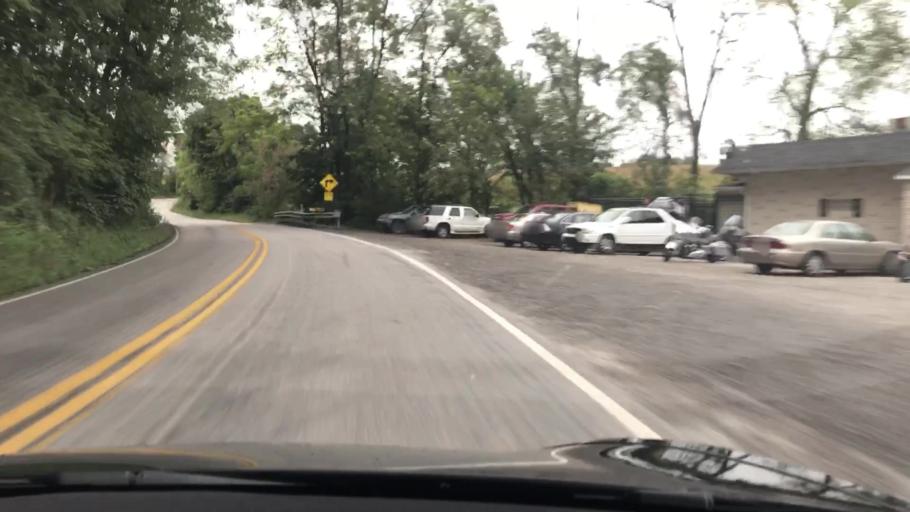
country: US
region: Pennsylvania
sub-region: York County
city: Weigelstown
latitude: 39.9465
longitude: -76.8614
